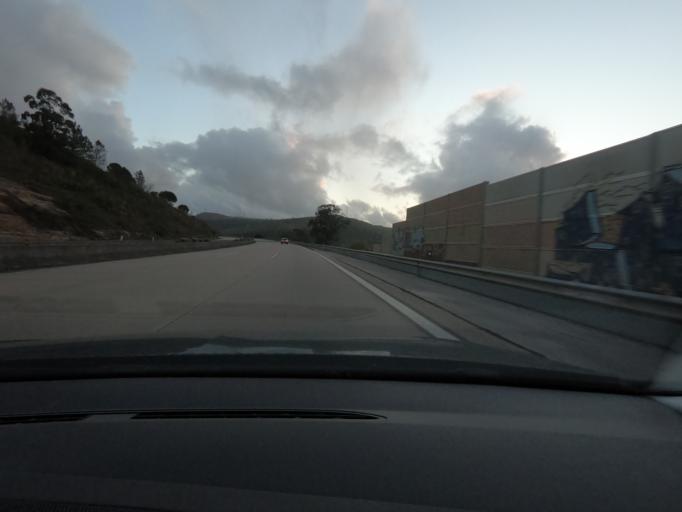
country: PT
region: Lisbon
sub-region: Loures
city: Bucelas
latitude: 38.8990
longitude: -9.1109
